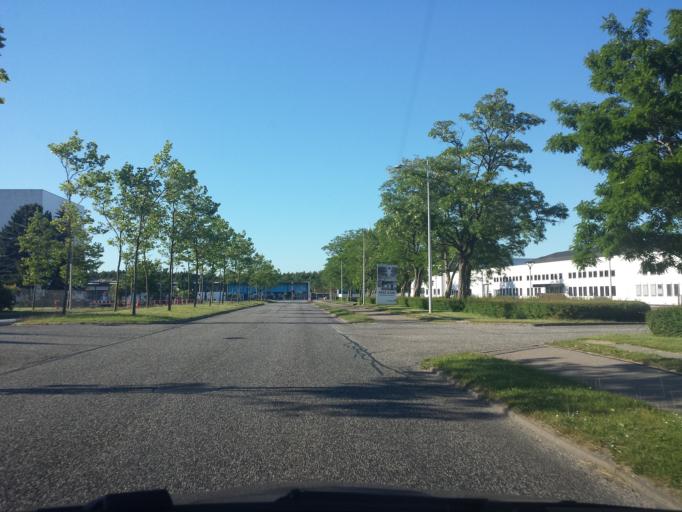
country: DK
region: Capital Region
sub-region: Glostrup Kommune
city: Glostrup
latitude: 55.6830
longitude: 12.3906
